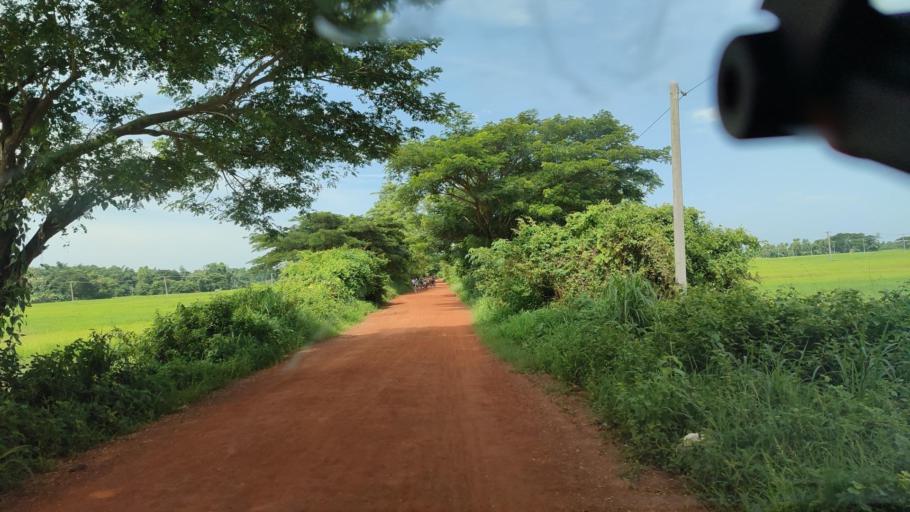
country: MM
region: Ayeyarwady
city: Hinthada
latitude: 17.6900
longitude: 95.5035
